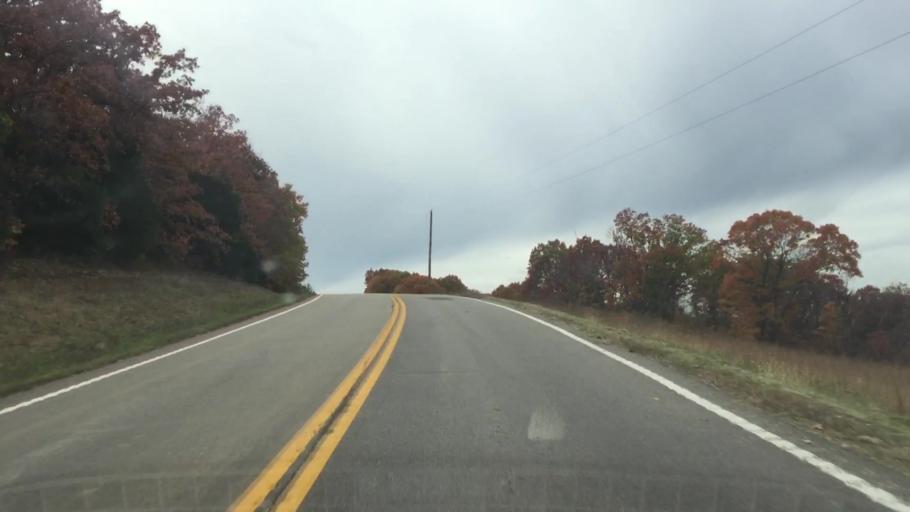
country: US
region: Missouri
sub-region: Gasconade County
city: Hermann
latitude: 38.7136
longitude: -91.6372
